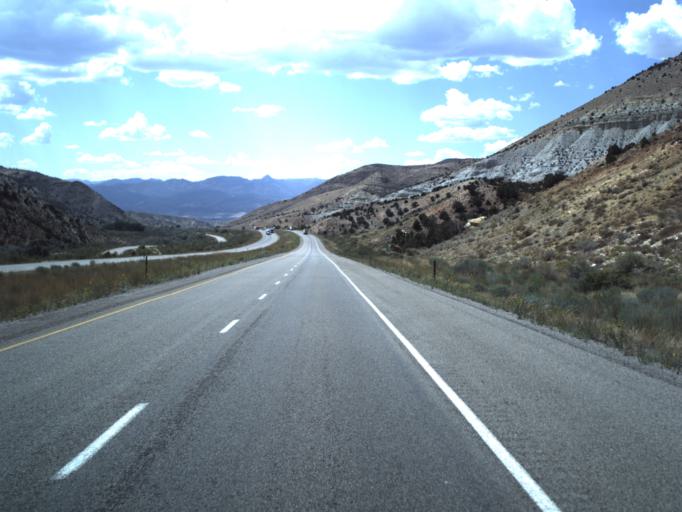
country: US
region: Utah
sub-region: Sevier County
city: Salina
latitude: 38.9329
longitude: -111.7929
